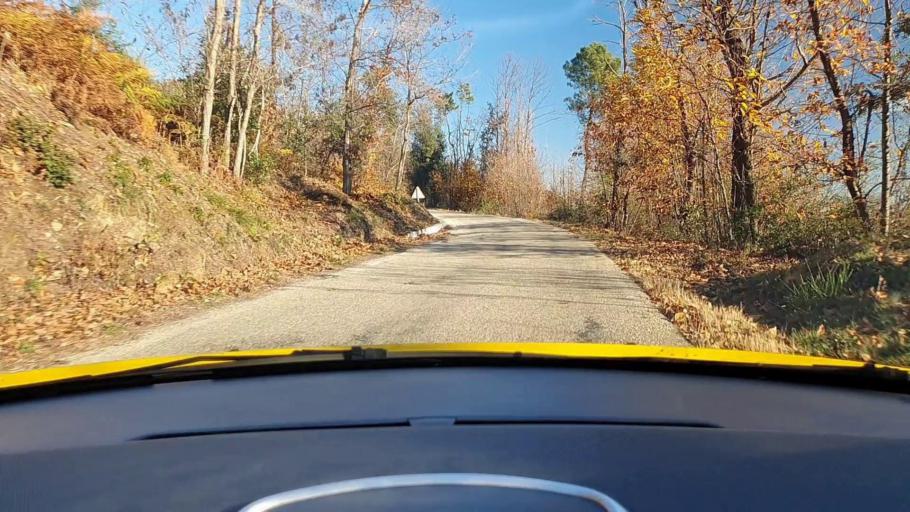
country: FR
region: Languedoc-Roussillon
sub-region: Departement du Gard
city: Branoux-les-Taillades
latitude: 44.2193
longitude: 3.9795
